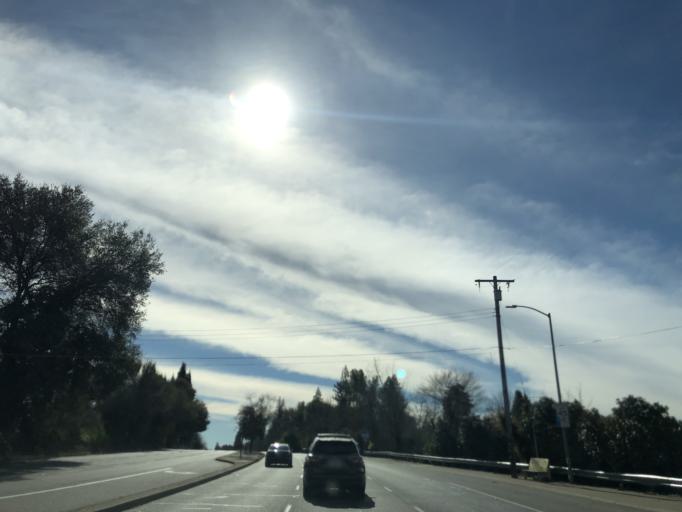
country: US
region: California
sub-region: Sacramento County
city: Fair Oaks
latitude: 38.6526
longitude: -121.2725
